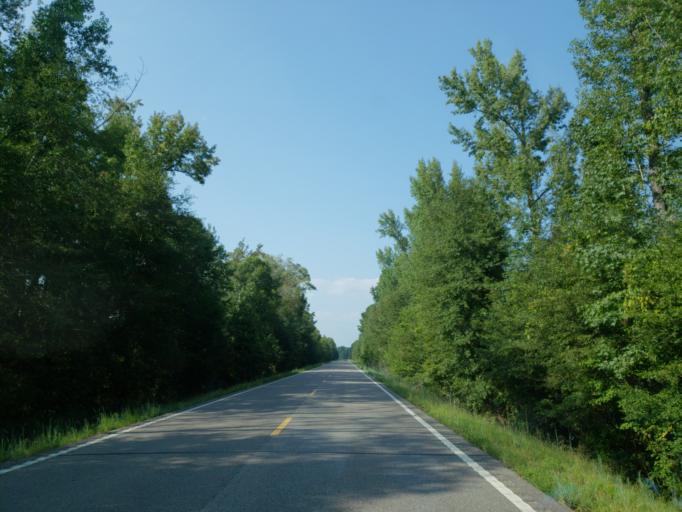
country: US
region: Mississippi
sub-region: Clarke County
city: Stonewall
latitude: 32.2541
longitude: -88.7703
